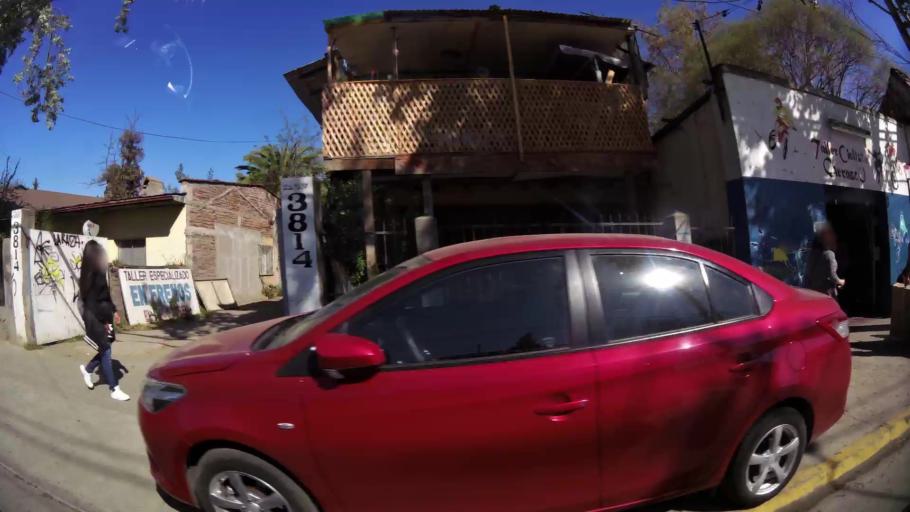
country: CL
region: Santiago Metropolitan
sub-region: Provincia de Talagante
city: Penaflor
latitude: -33.6067
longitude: -70.8958
